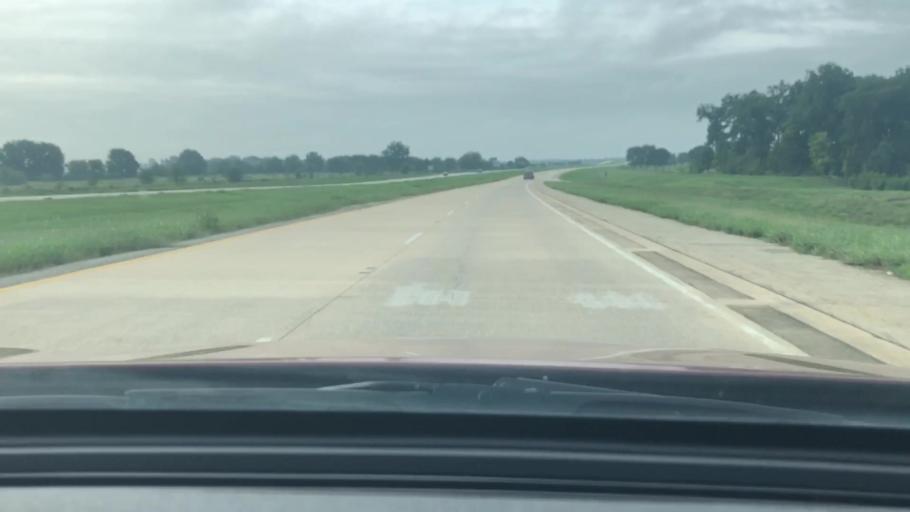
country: US
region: Louisiana
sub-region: Caddo Parish
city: Vivian
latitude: 32.8945
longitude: -93.8610
